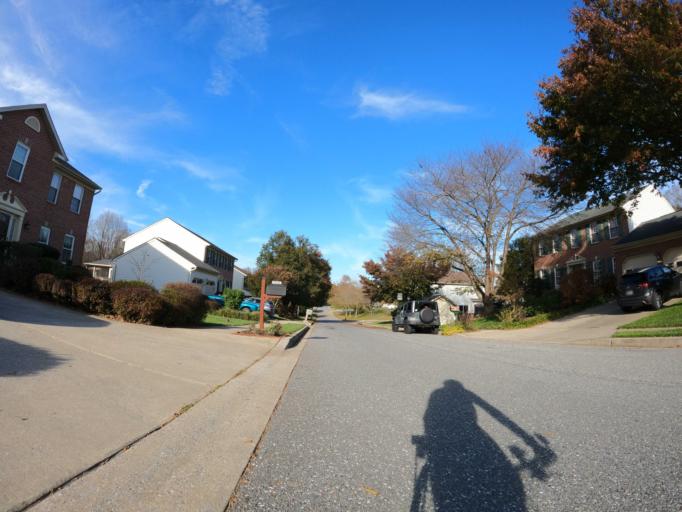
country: US
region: Maryland
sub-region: Carroll County
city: Sykesville
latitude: 39.3677
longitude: -76.9814
